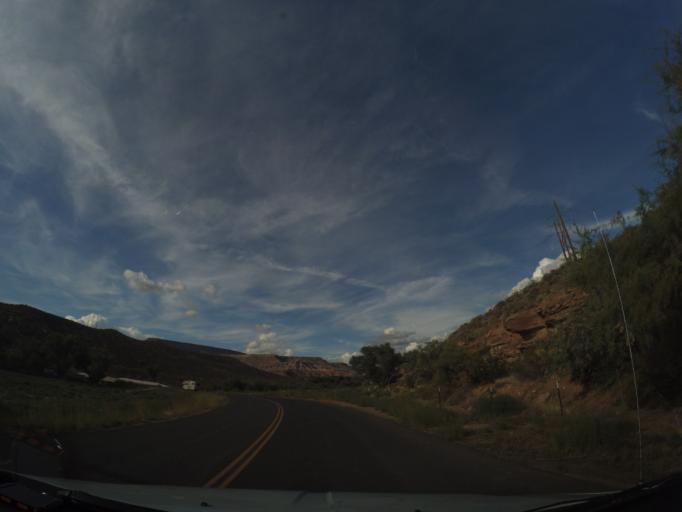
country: US
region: Utah
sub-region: Washington County
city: LaVerkin
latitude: 37.2038
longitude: -113.1710
